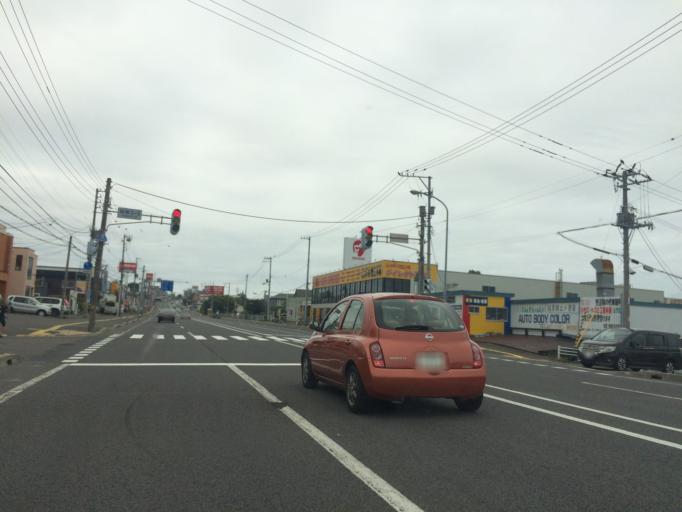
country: JP
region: Hokkaido
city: Sapporo
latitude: 43.1244
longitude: 141.2225
